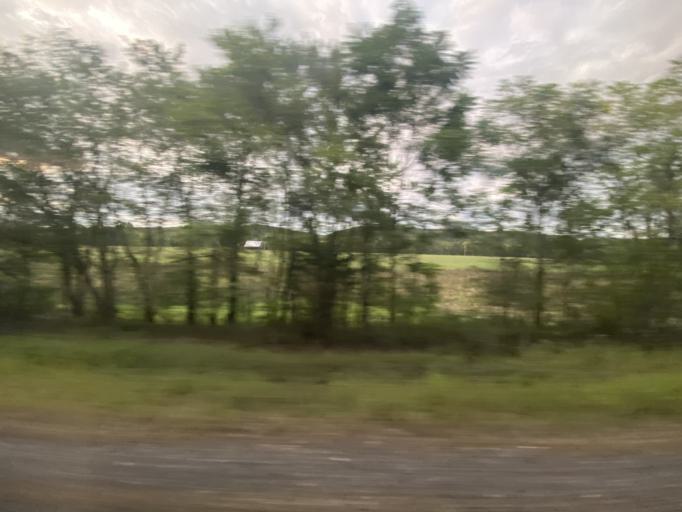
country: US
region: West Virginia
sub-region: Mineral County
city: Fort Ashby
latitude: 39.5172
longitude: -78.5599
